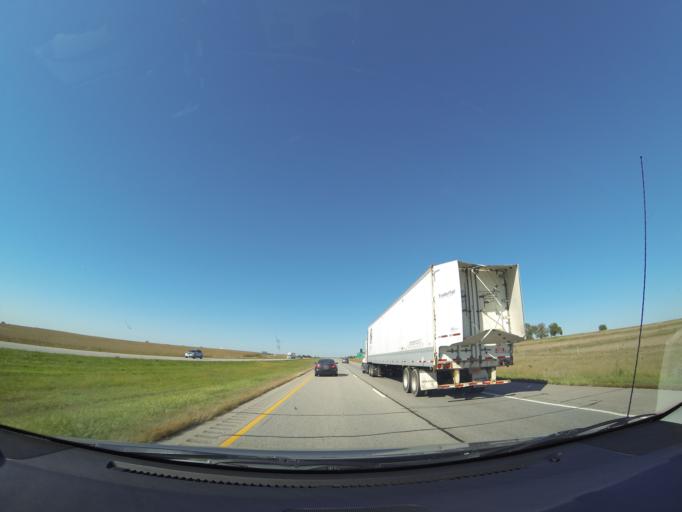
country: US
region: Nebraska
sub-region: Seward County
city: Milford
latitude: 40.8223
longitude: -97.0904
